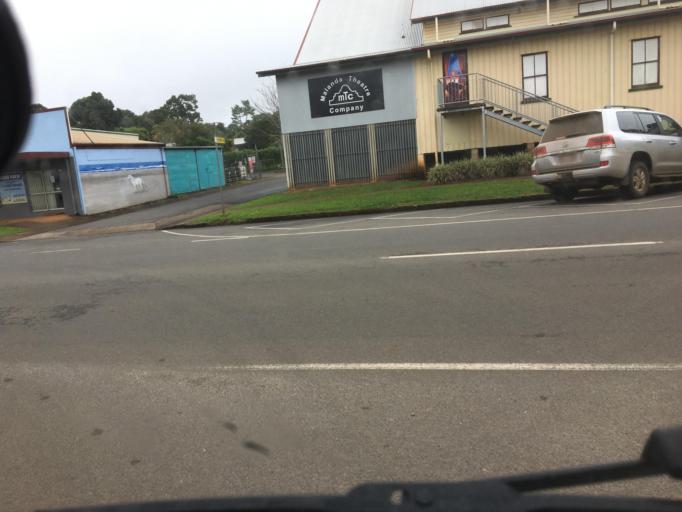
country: AU
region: Queensland
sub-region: Tablelands
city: Atherton
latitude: -17.3533
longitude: 145.5931
